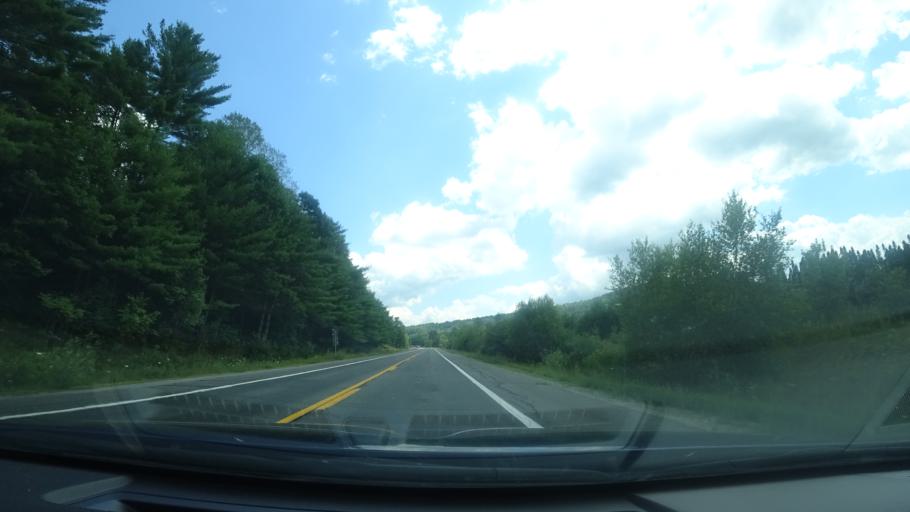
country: US
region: New York
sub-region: Warren County
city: Warrensburg
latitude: 43.6559
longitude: -73.8081
